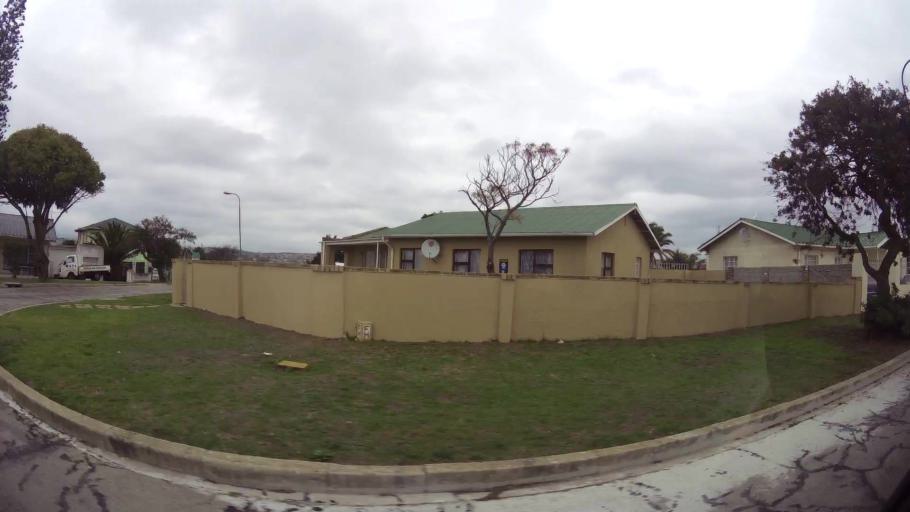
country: ZA
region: Eastern Cape
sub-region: Nelson Mandela Bay Metropolitan Municipality
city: Port Elizabeth
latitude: -33.9058
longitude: 25.5643
